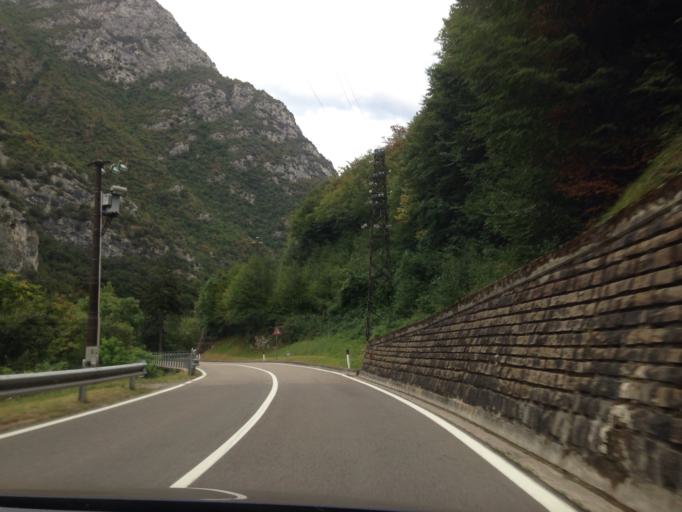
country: IT
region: Trentino-Alto Adige
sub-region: Provincia di Trento
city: Riva del Garda
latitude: 45.8637
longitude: 10.8158
